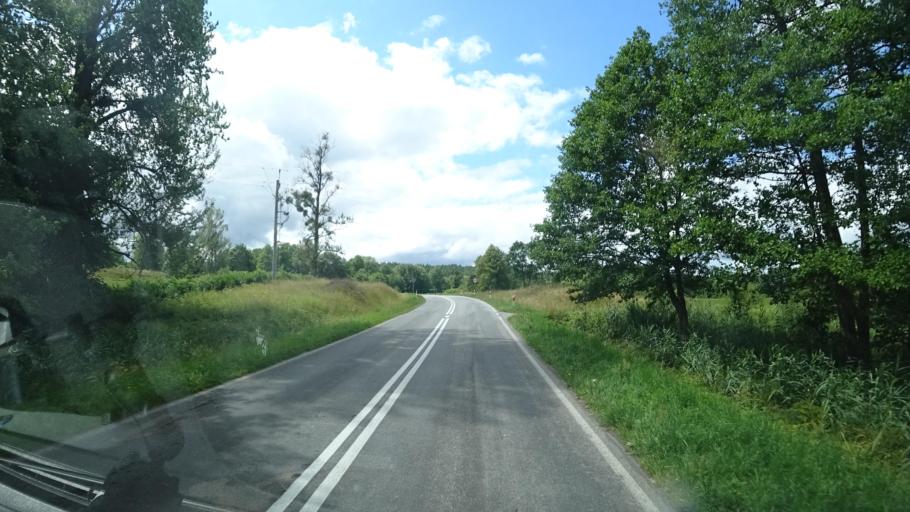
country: PL
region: Warmian-Masurian Voivodeship
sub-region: Powiat goldapski
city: Banie Mazurskie
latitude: 54.2148
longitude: 22.1615
